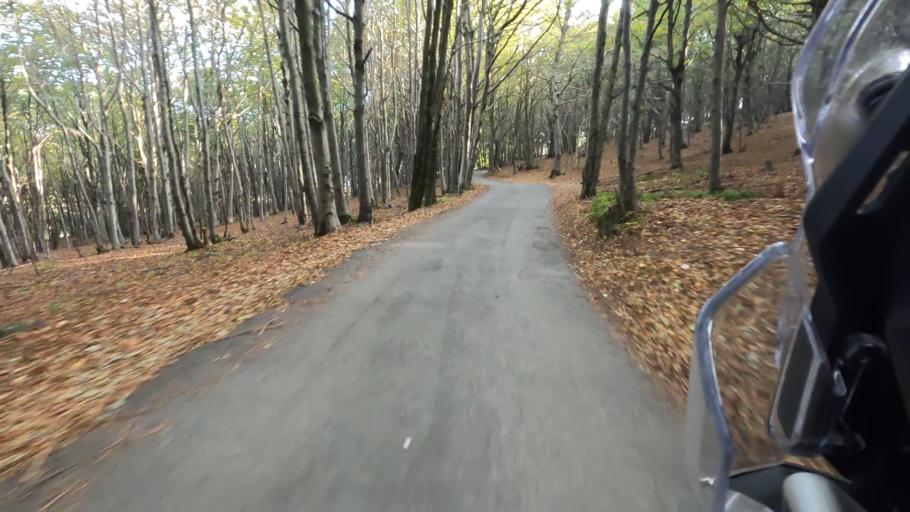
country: IT
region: Liguria
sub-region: Provincia di Genova
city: Sciarborasca
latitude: 44.4305
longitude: 8.5866
